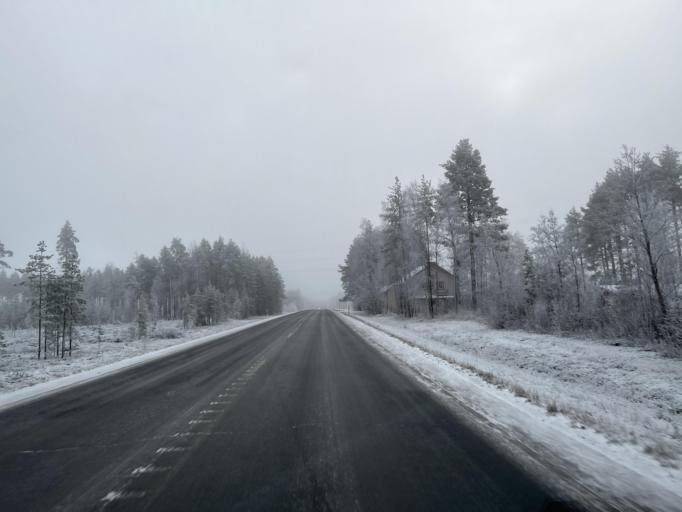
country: FI
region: Northern Ostrobothnia
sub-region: Oulunkaari
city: Utajaervi
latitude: 64.7379
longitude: 26.4642
